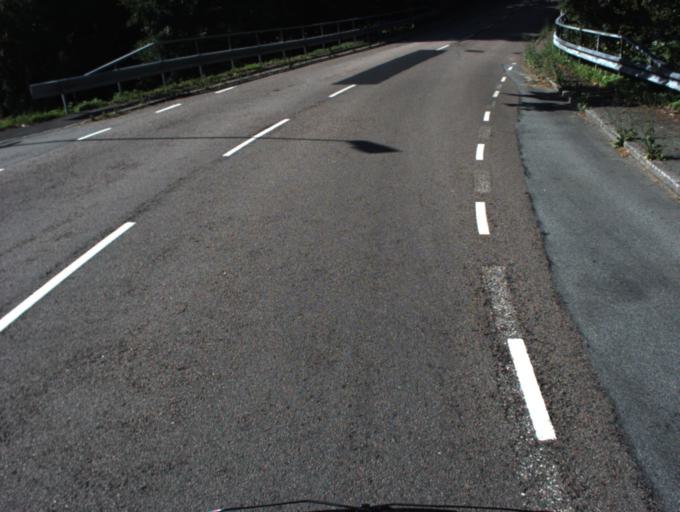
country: DK
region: Capital Region
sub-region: Helsingor Kommune
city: Helsingor
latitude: 56.0970
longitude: 12.6433
